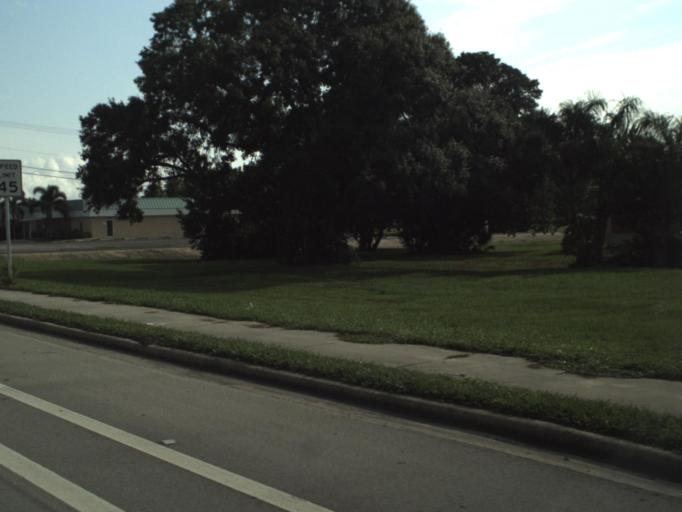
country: US
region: Florida
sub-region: Palm Beach County
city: Belle Glade
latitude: 26.6706
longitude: -80.6705
